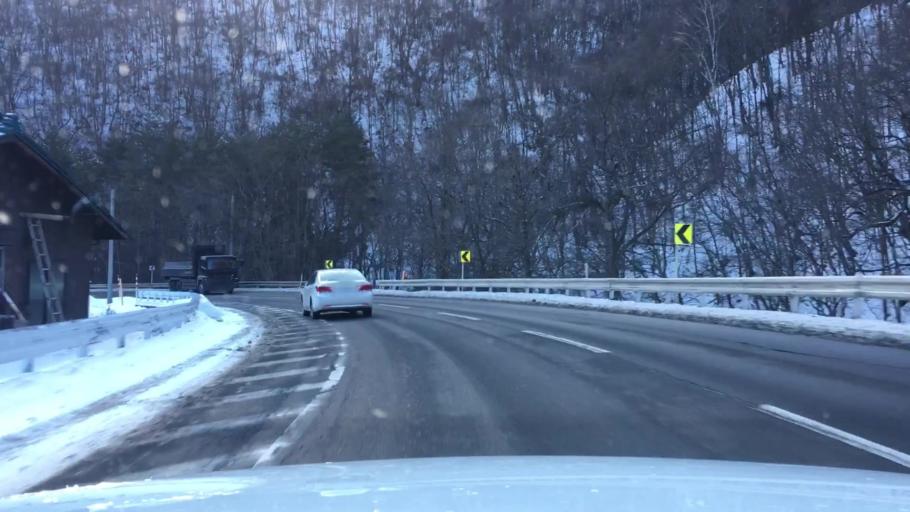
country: JP
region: Iwate
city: Tono
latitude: 39.6151
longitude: 141.4754
